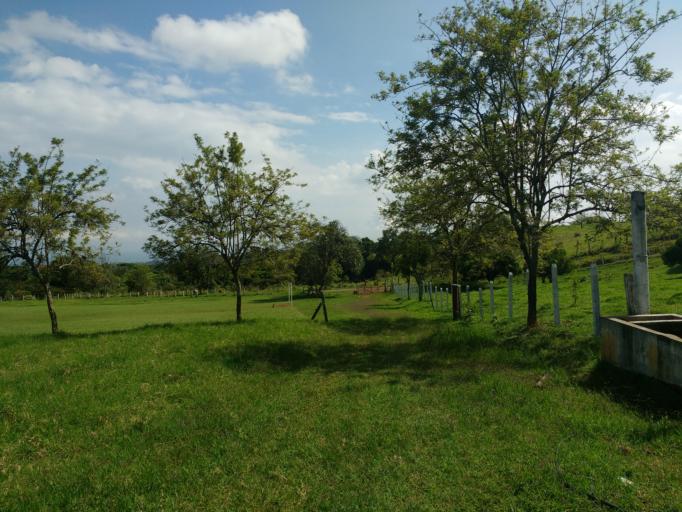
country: CO
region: Cauca
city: Santander de Quilichao
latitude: 2.9827
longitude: -76.4539
